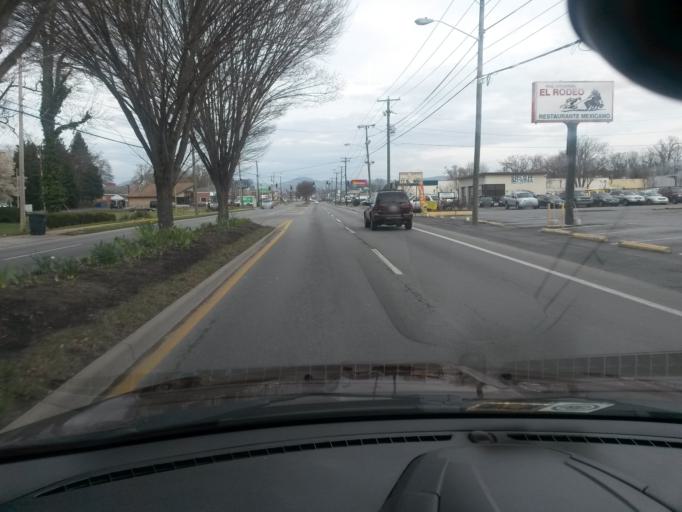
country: US
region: Virginia
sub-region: Roanoke County
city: Hollins
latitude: 37.3095
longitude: -79.9491
